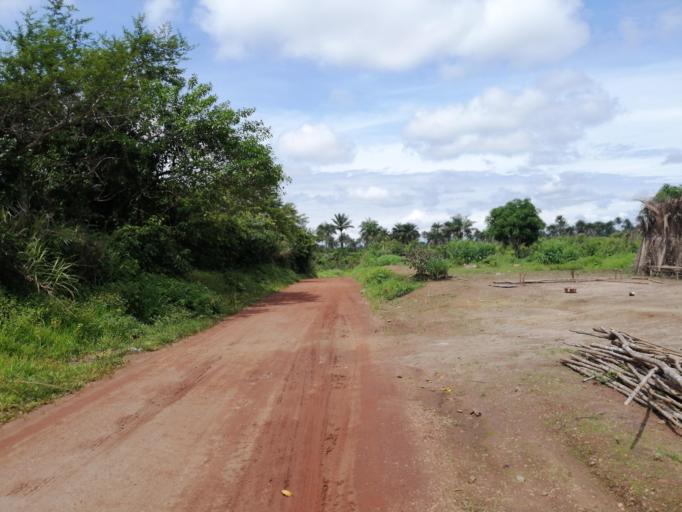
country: SL
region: Northern Province
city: Pepel
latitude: 8.6524
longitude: -13.0082
